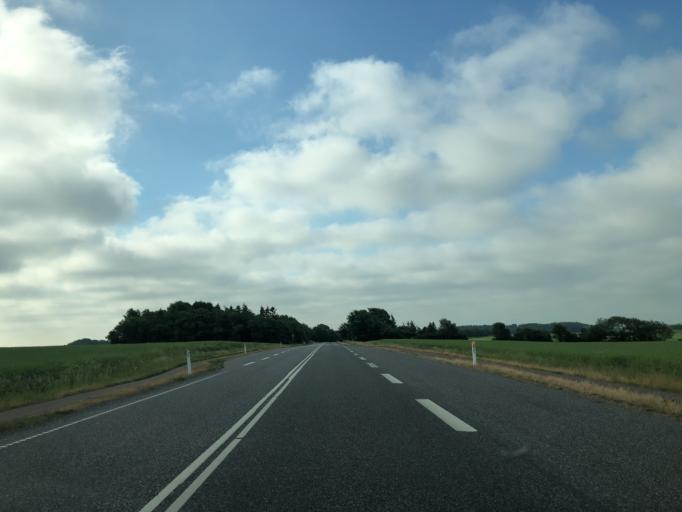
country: DK
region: South Denmark
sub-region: Vejle Kommune
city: Jelling
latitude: 55.7296
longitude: 9.3600
